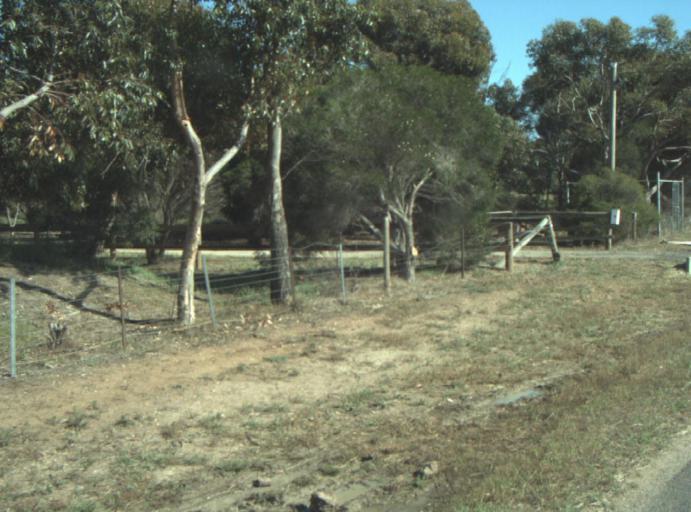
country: AU
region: Victoria
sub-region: Wyndham
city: Little River
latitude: -37.9755
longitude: 144.4608
